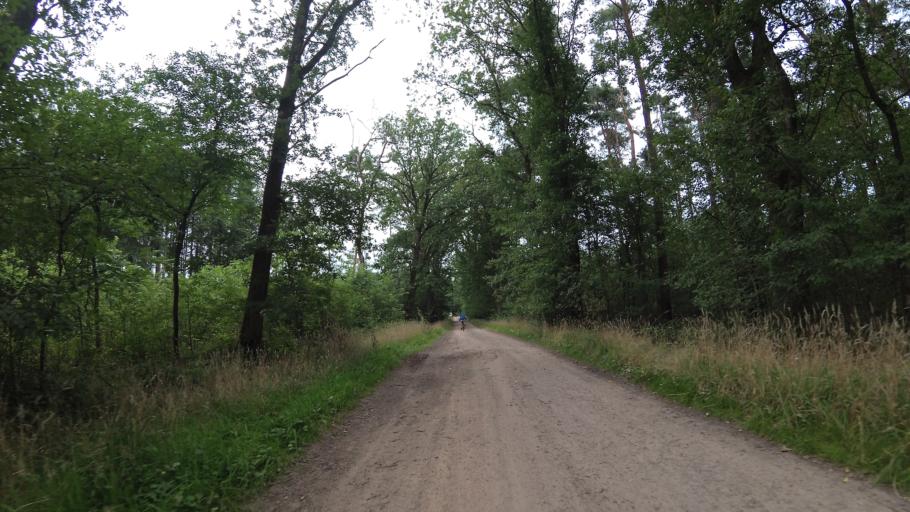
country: DE
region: Lower Saxony
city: Fresenburg
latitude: 52.8763
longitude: 7.2986
